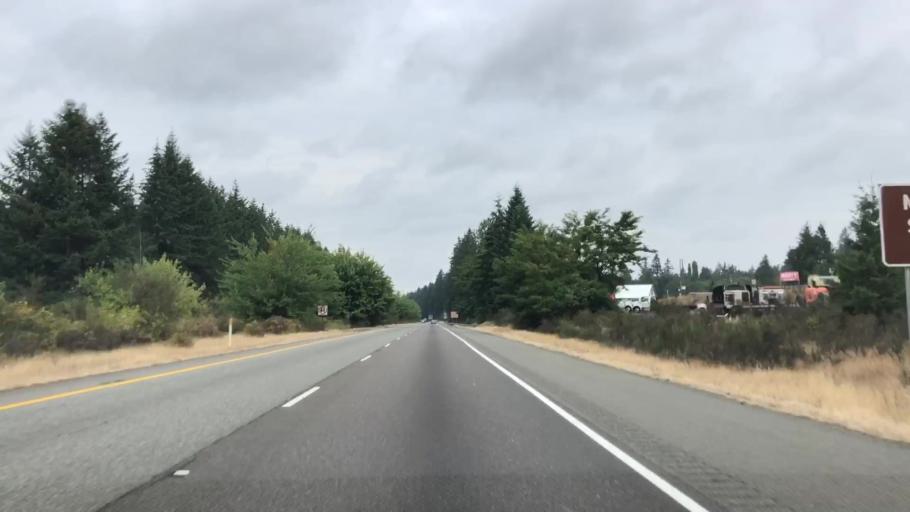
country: US
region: Washington
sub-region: Kitsap County
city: Bethel
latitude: 47.4860
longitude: -122.6314
